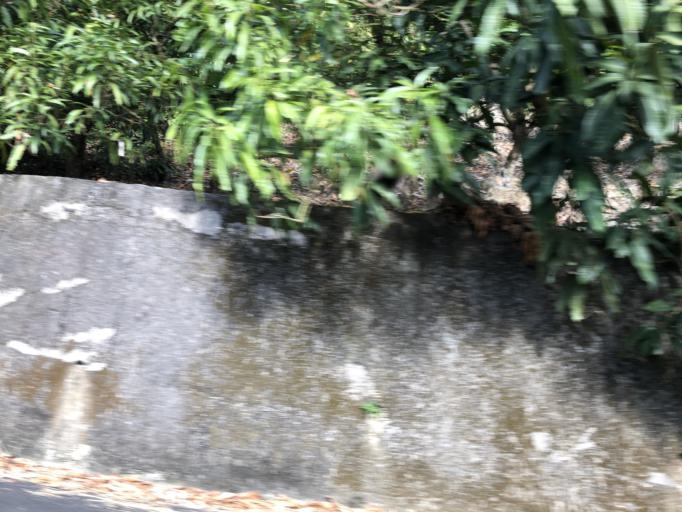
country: TW
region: Taiwan
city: Yujing
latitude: 23.0274
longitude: 120.3946
